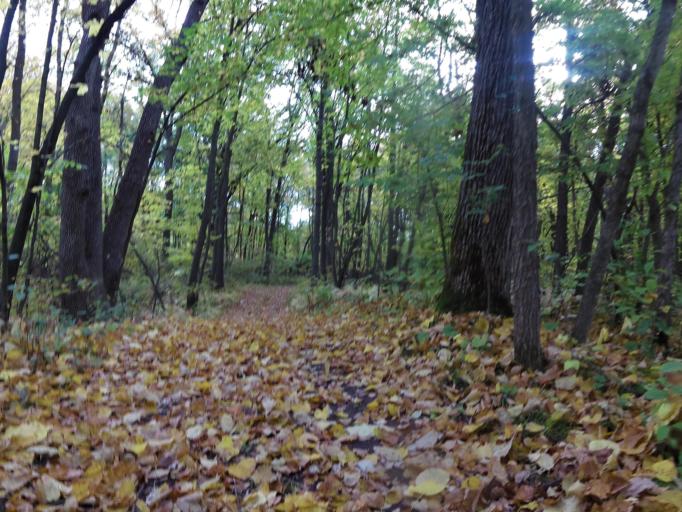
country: US
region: North Dakota
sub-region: Pembina County
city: Cavalier
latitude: 48.7785
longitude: -97.7339
